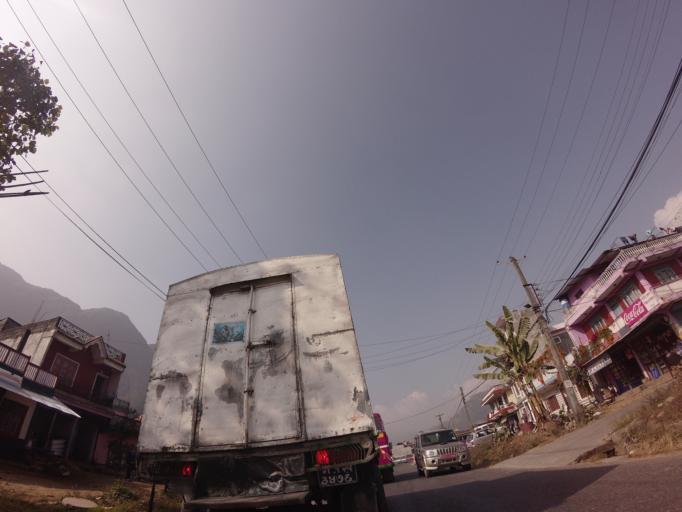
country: NP
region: Western Region
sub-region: Gandaki Zone
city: Pokhara
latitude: 28.2783
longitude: 83.9328
